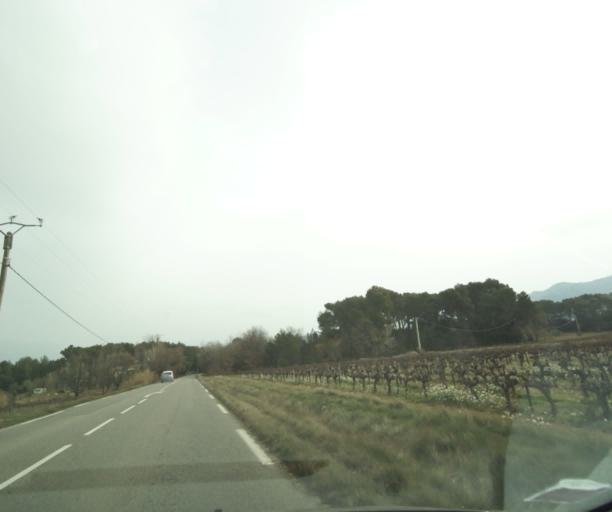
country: FR
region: Provence-Alpes-Cote d'Azur
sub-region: Departement des Bouches-du-Rhone
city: Trets
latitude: 43.4628
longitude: 5.7196
